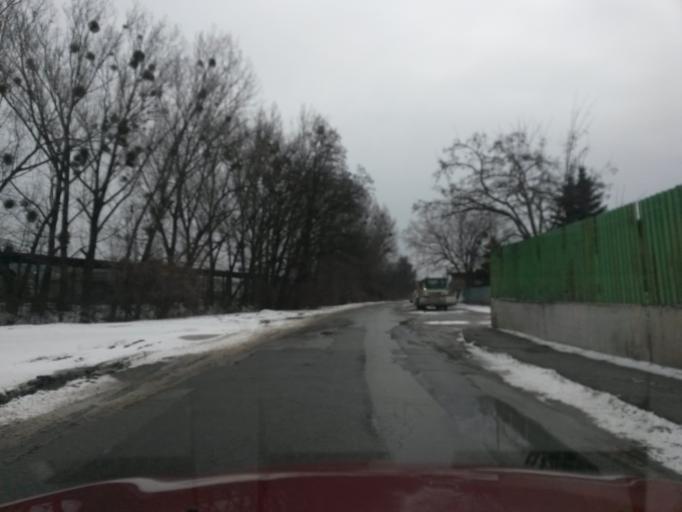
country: SK
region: Kosicky
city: Kosice
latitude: 48.7126
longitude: 21.2690
